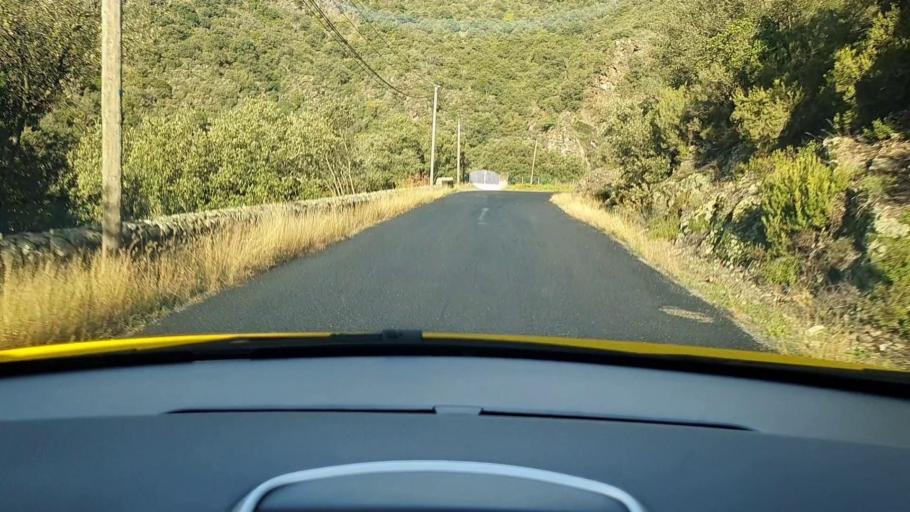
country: FR
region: Languedoc-Roussillon
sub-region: Departement du Gard
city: Sumene
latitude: 44.0135
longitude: 3.7180
